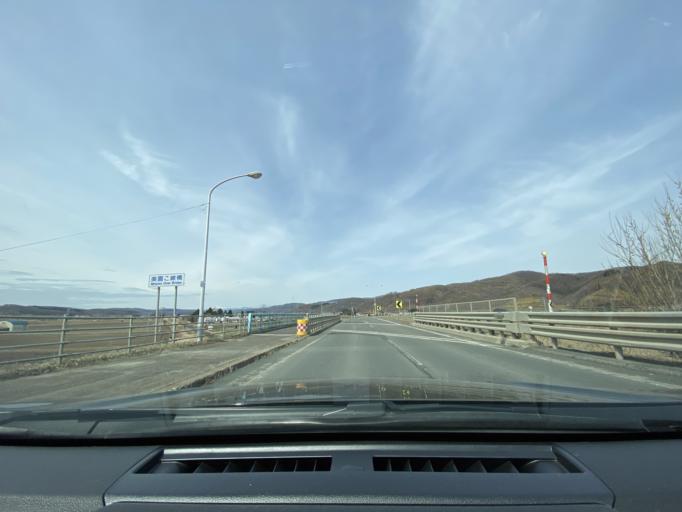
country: JP
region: Hokkaido
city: Kitami
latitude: 43.8009
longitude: 143.7824
